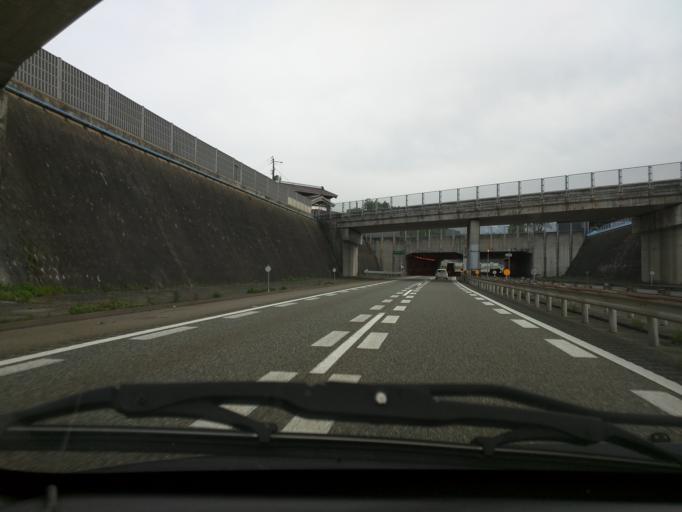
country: JP
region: Niigata
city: Ojiya
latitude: 37.2323
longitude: 138.9761
